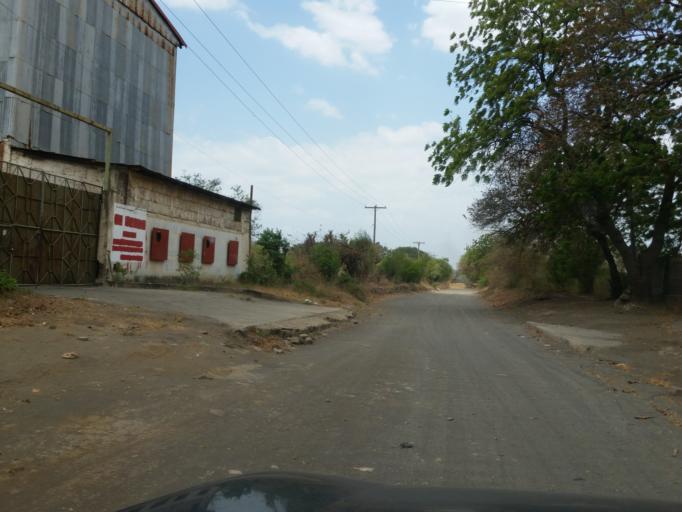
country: NI
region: Managua
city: Managua
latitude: 12.1314
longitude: -86.1642
